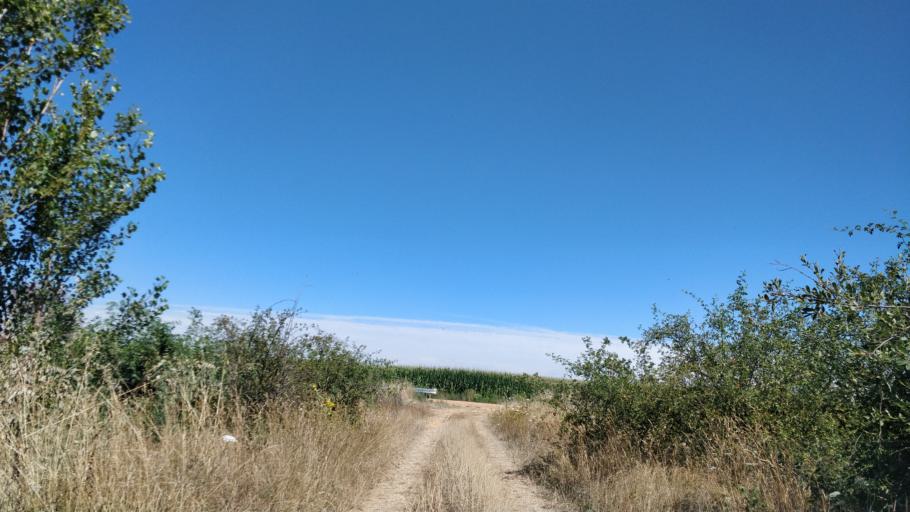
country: ES
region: Castille and Leon
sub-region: Provincia de Leon
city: Bustillo del Paramo
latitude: 42.4514
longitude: -5.8174
